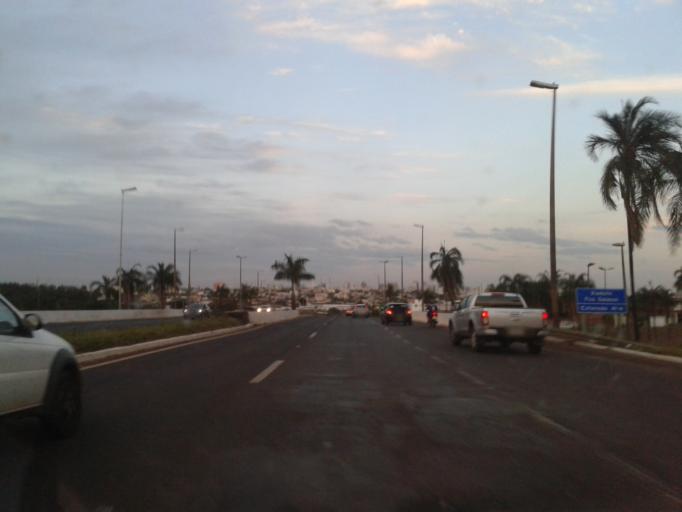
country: BR
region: Minas Gerais
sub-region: Uberlandia
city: Uberlandia
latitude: -18.9082
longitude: -48.3134
